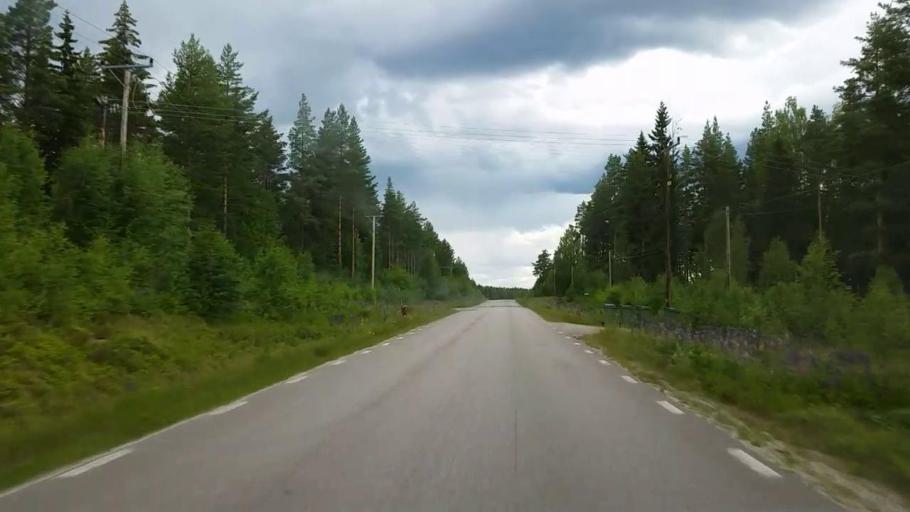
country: SE
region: Gaevleborg
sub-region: Ovanakers Kommun
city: Edsbyn
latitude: 61.4666
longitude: 15.8677
